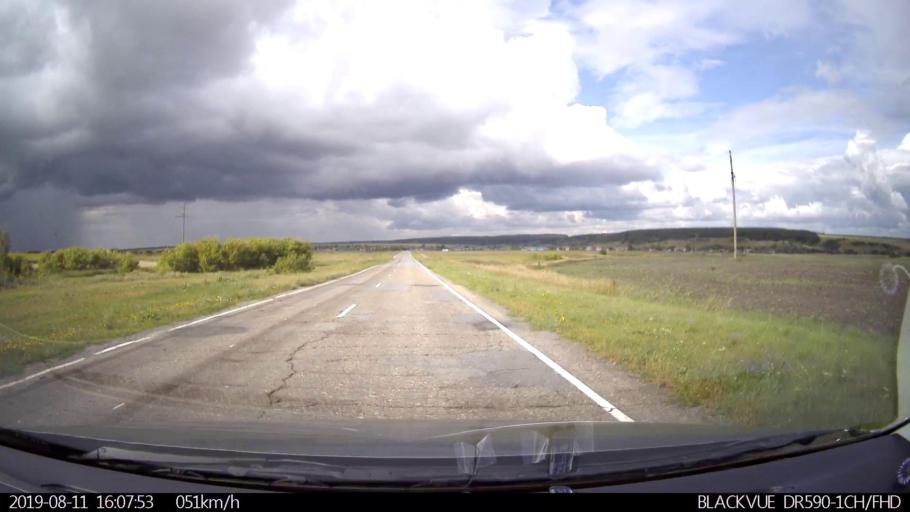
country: RU
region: Ulyanovsk
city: Ignatovka
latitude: 53.9805
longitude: 47.6469
